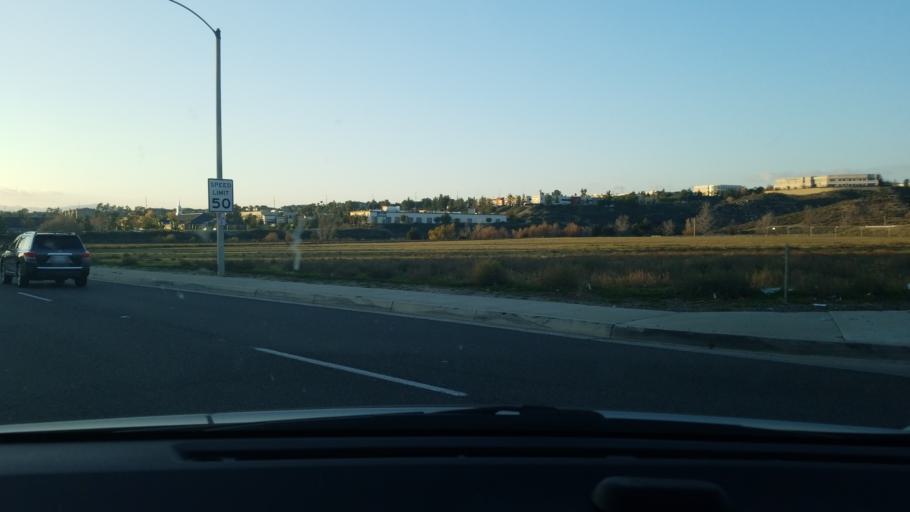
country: US
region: California
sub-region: Riverside County
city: Murrieta Hot Springs
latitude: 33.5523
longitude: -117.1325
